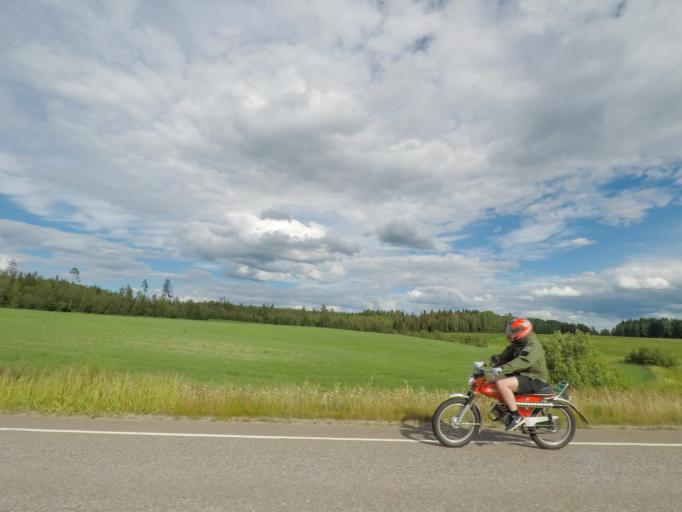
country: FI
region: Paijanne Tavastia
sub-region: Lahti
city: Hollola
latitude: 60.8244
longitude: 25.4877
